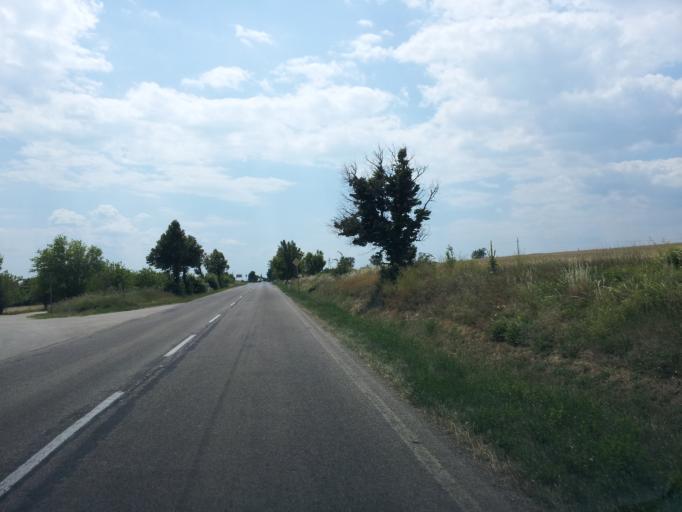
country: HU
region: Veszprem
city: Balatonfured
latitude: 46.9250
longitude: 17.8283
